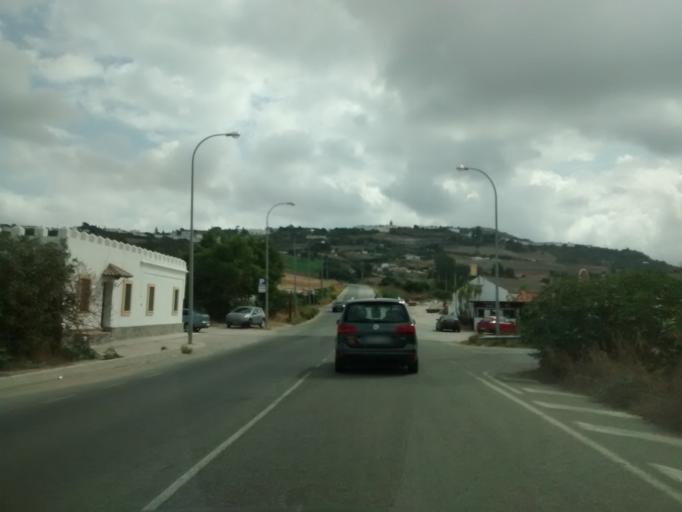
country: ES
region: Andalusia
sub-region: Provincia de Cadiz
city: Medina Sidonia
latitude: 36.4575
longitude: -5.9441
